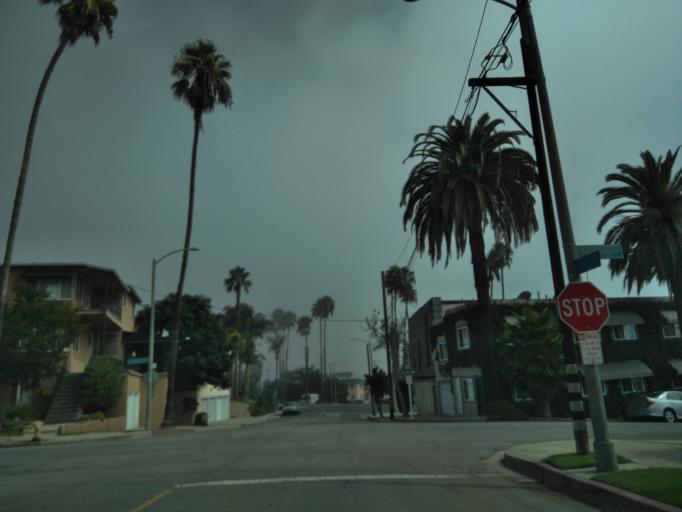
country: US
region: California
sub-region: Los Angeles County
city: Long Beach
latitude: 33.7610
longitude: -118.1461
